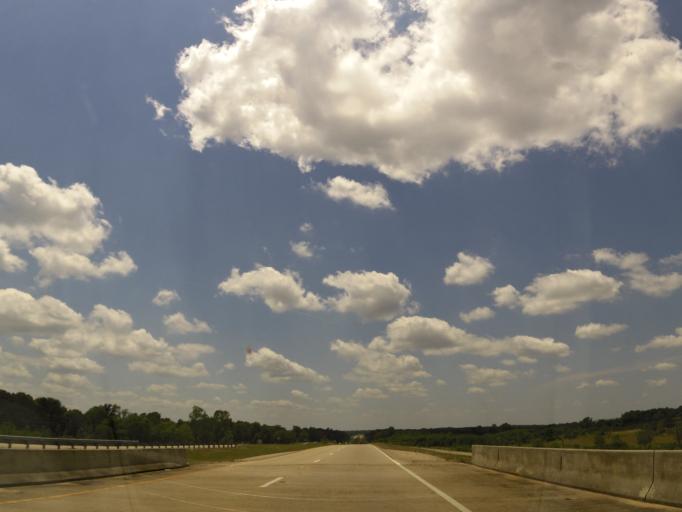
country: US
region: Mississippi
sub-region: Pontotoc County
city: Pontotoc
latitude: 34.2869
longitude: -89.0263
